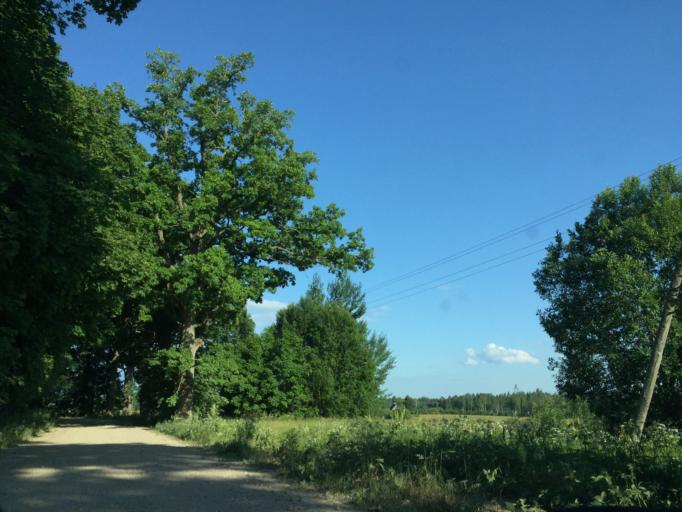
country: LV
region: Aizkraukles Rajons
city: Aizkraukle
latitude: 56.7896
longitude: 25.2679
